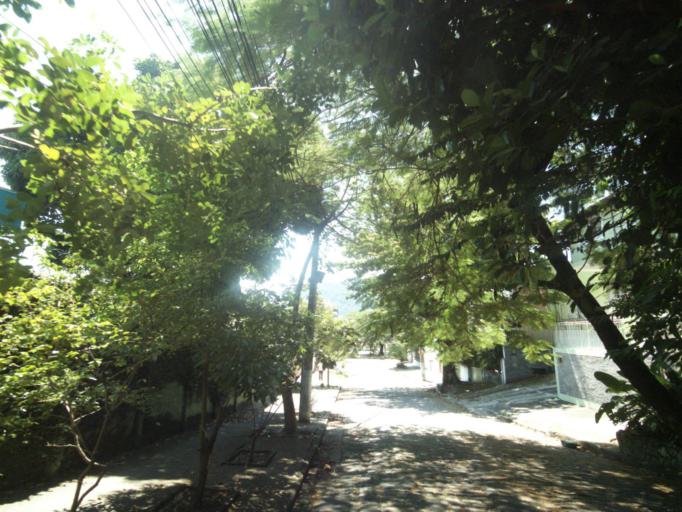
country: BR
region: Rio de Janeiro
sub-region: Niteroi
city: Niteroi
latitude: -22.9224
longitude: -43.0906
